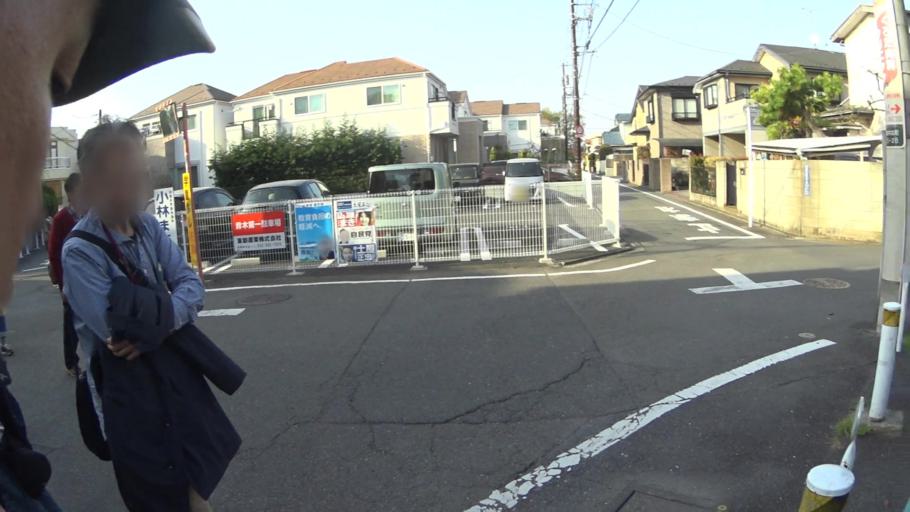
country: JP
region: Tokyo
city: Kokubunji
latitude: 35.7107
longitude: 139.5012
